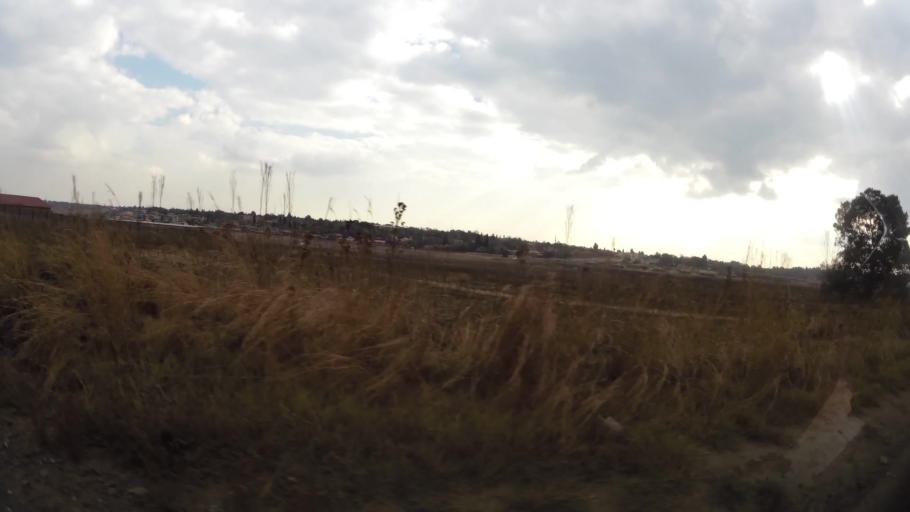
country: ZA
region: Gauteng
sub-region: Ekurhuleni Metropolitan Municipality
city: Benoni
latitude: -26.1385
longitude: 28.3568
